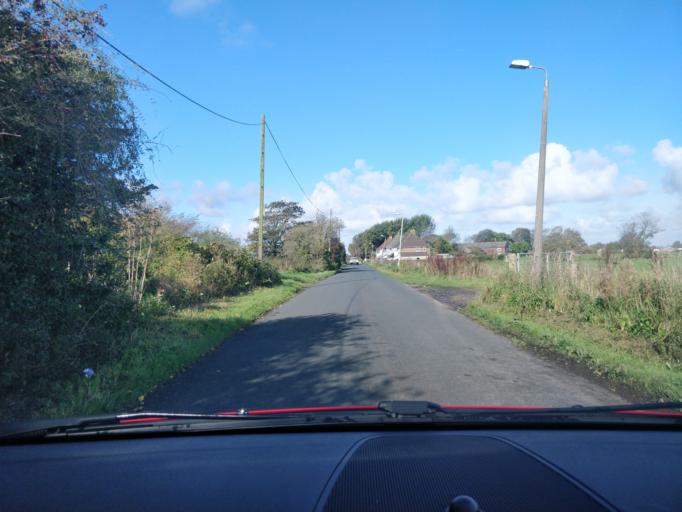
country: GB
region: England
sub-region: Lancashire
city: Banks
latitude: 53.6236
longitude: -2.9393
